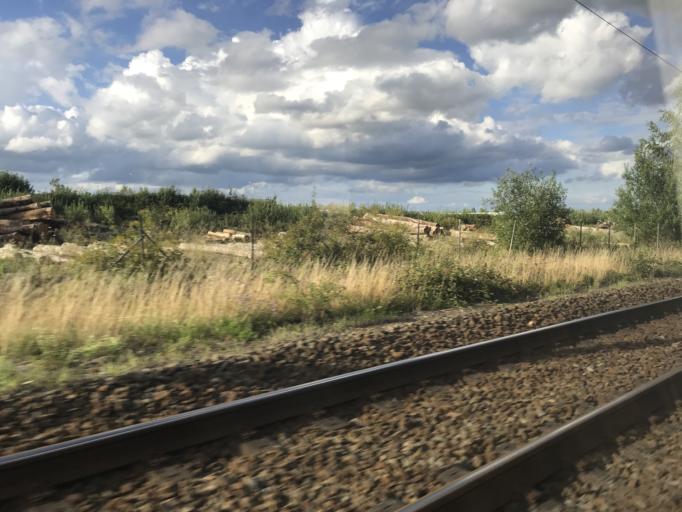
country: FR
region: Champagne-Ardenne
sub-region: Departement des Ardennes
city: Bazeilles
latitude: 49.6723
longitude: 4.9884
